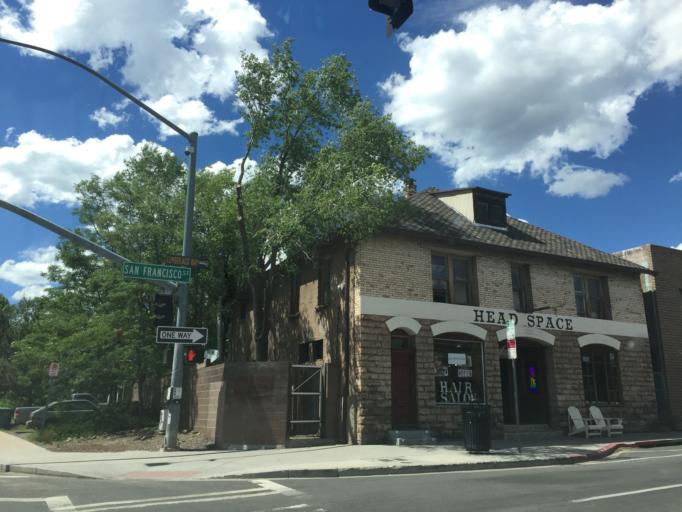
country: US
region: Arizona
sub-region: Coconino County
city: Flagstaff
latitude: 35.1937
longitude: -111.6496
